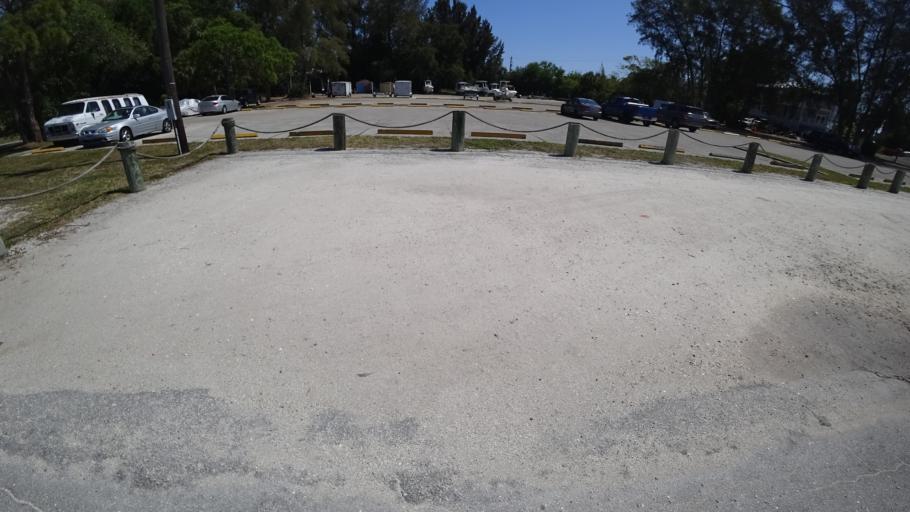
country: US
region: Florida
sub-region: Manatee County
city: Cortez
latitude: 27.4710
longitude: -82.6899
